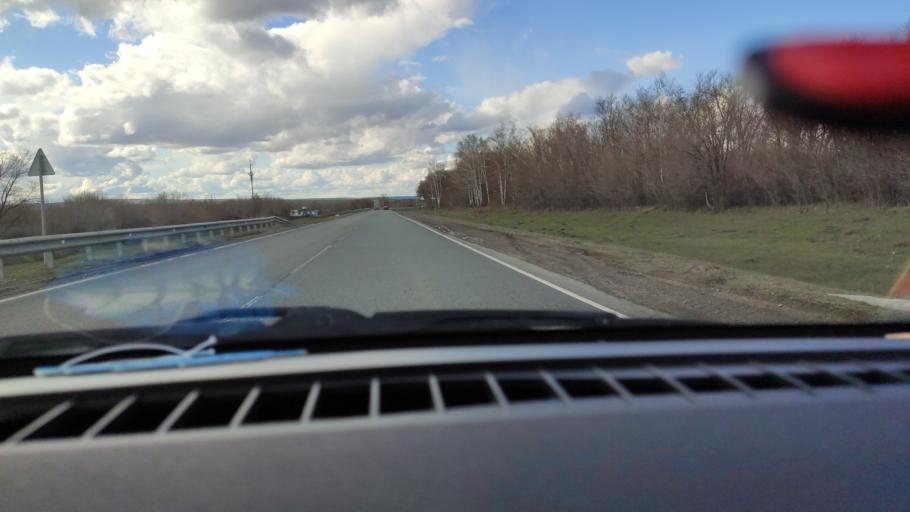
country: RU
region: Saratov
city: Tersa
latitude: 52.0897
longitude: 47.5463
